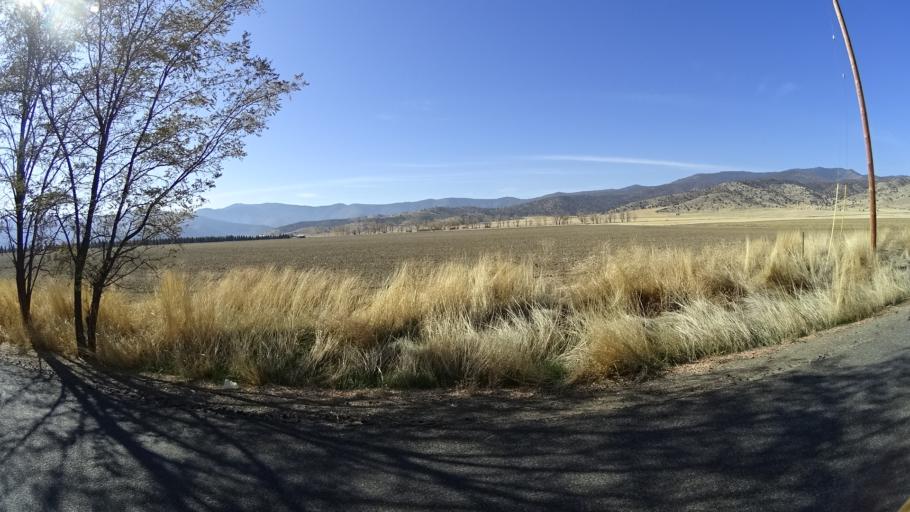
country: US
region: California
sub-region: Siskiyou County
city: Montague
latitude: 41.5593
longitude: -122.5468
